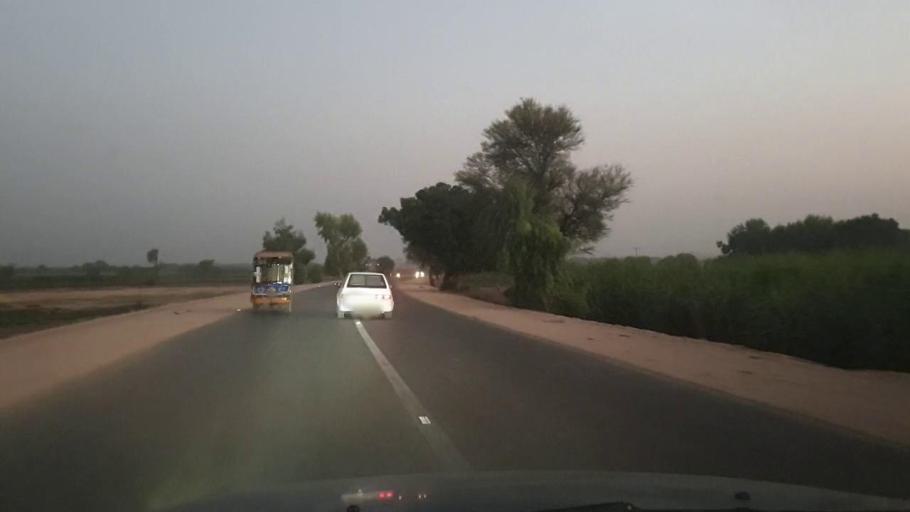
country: PK
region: Sindh
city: Tando Allahyar
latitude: 25.4298
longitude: 68.7487
